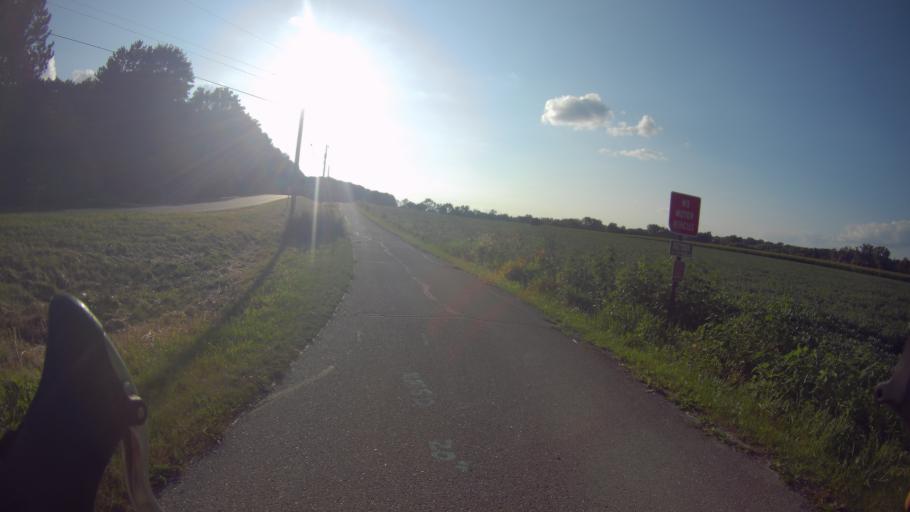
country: US
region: Wisconsin
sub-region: Dane County
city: Monona
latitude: 43.0226
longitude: -89.3654
